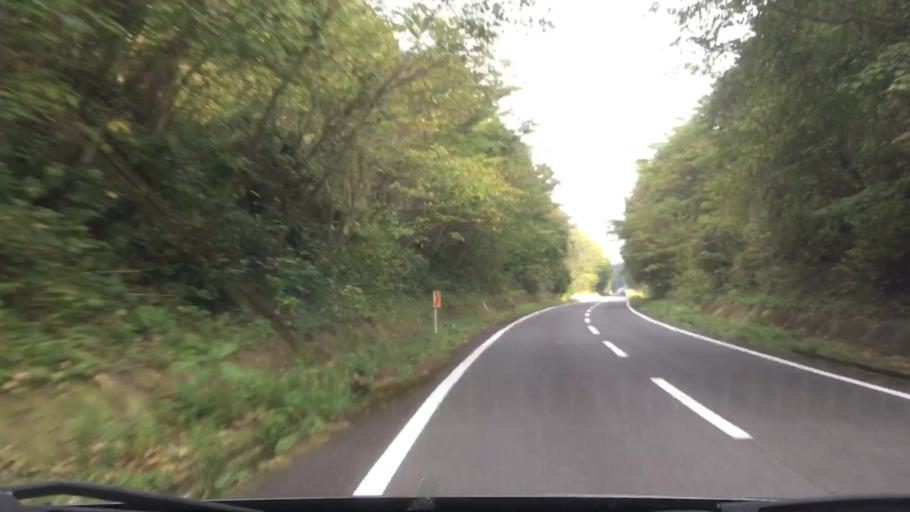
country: JP
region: Nagasaki
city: Sasebo
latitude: 32.9994
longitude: 129.7075
